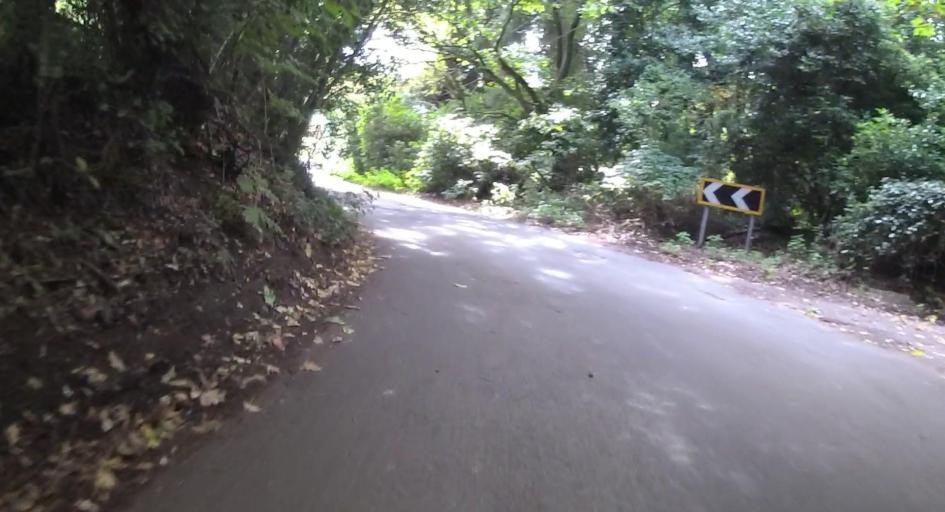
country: GB
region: England
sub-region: Surrey
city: Chobham
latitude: 51.3451
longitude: -0.6173
